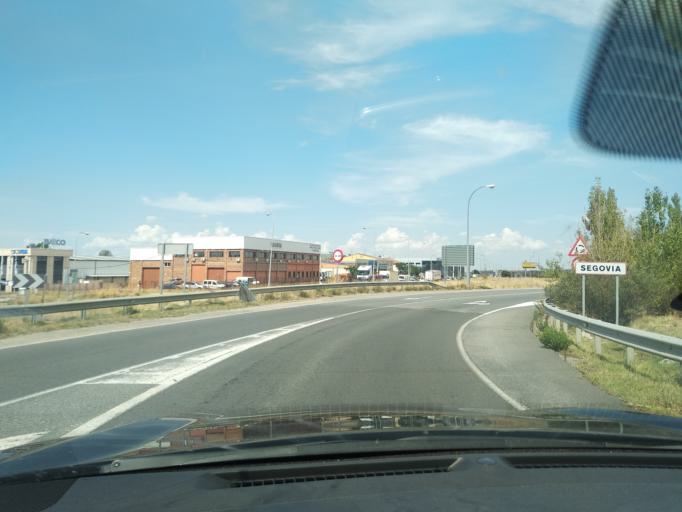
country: ES
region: Castille and Leon
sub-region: Provincia de Segovia
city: Segovia
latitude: 40.8999
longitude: -4.1029
